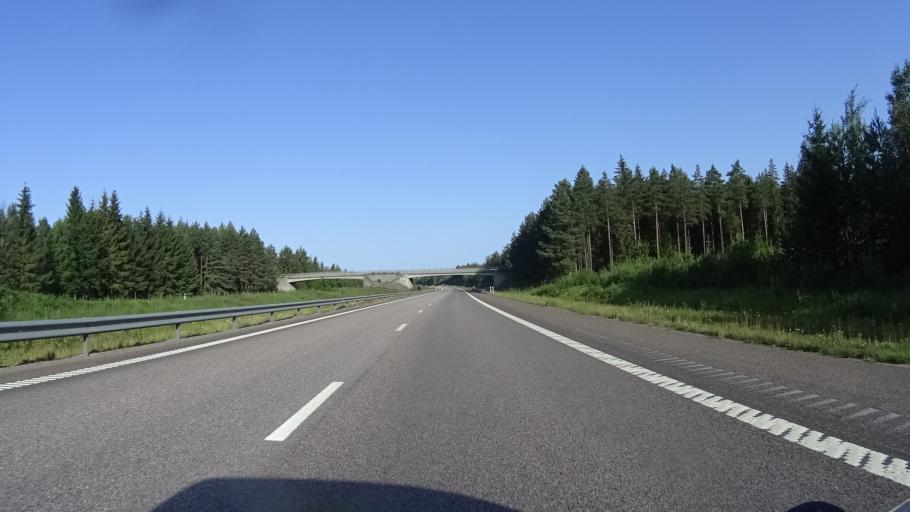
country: SE
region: Soedermanland
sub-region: Nykopings Kommun
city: Svalsta
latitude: 58.7574
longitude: 16.8187
